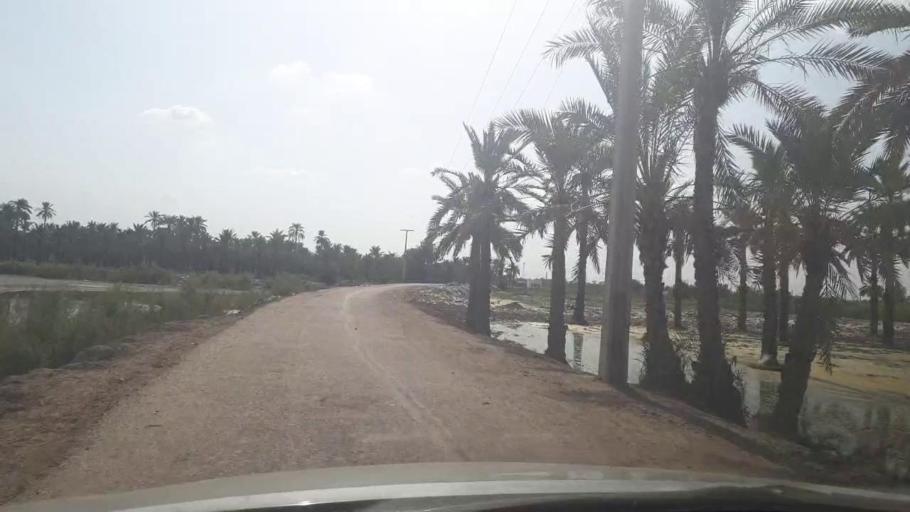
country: PK
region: Sindh
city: Khairpur
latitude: 27.5293
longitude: 68.7761
